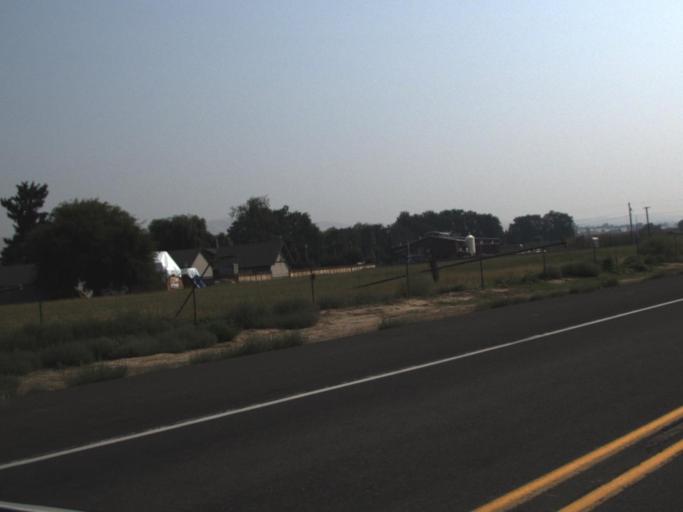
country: US
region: Washington
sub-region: Yakima County
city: Terrace Heights
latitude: 46.5762
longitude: -120.4396
